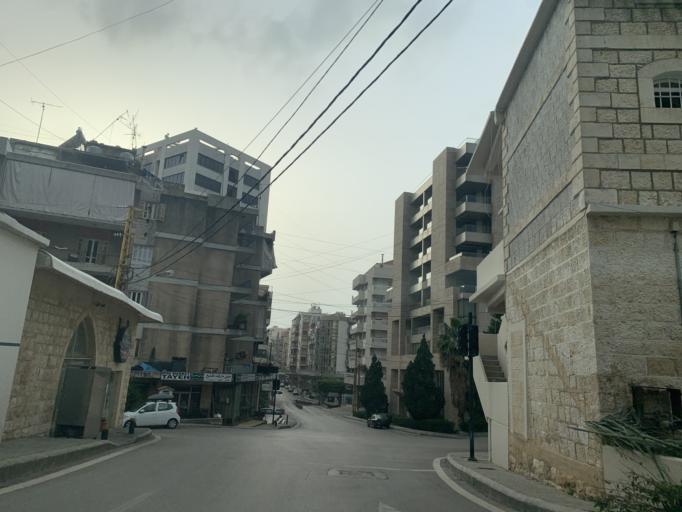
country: LB
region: Mont-Liban
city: Djounie
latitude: 33.9790
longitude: 35.6302
